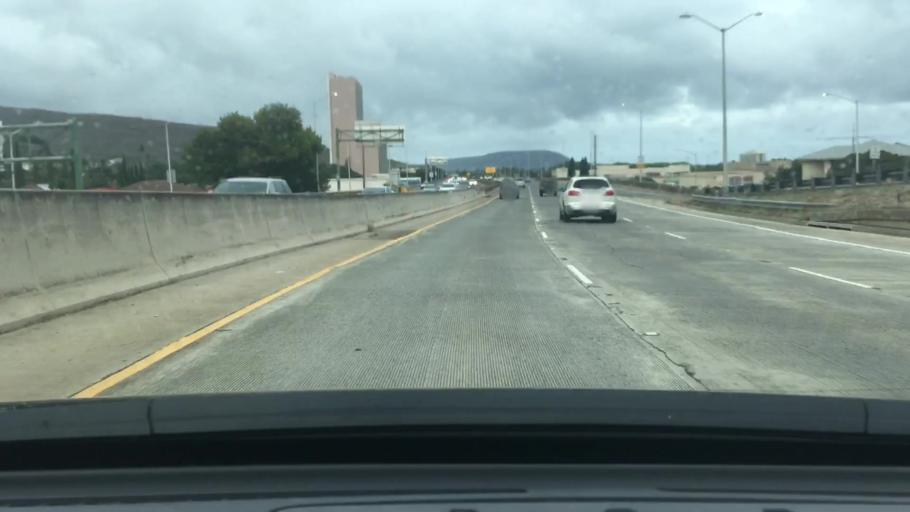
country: US
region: Hawaii
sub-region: Honolulu County
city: Honolulu
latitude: 21.2790
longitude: -157.7906
